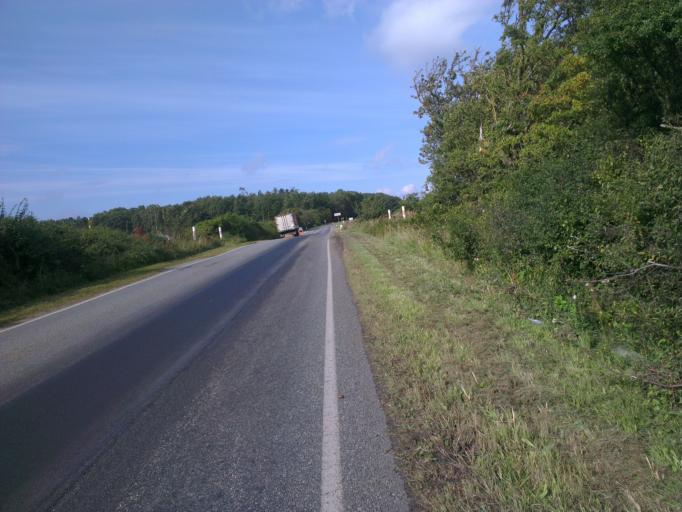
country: DK
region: Capital Region
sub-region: Frederikssund Kommune
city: Jaegerspris
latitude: 55.8736
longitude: 11.9580
